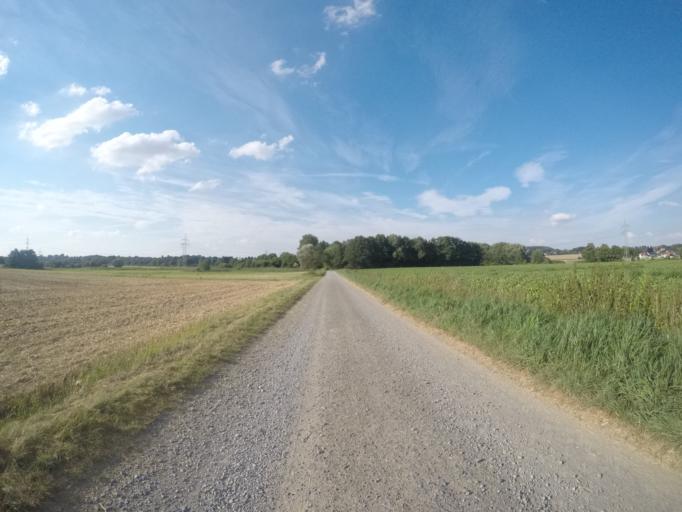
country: DE
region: North Rhine-Westphalia
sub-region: Regierungsbezirk Detmold
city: Hiddenhausen
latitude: 52.1353
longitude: 8.6322
